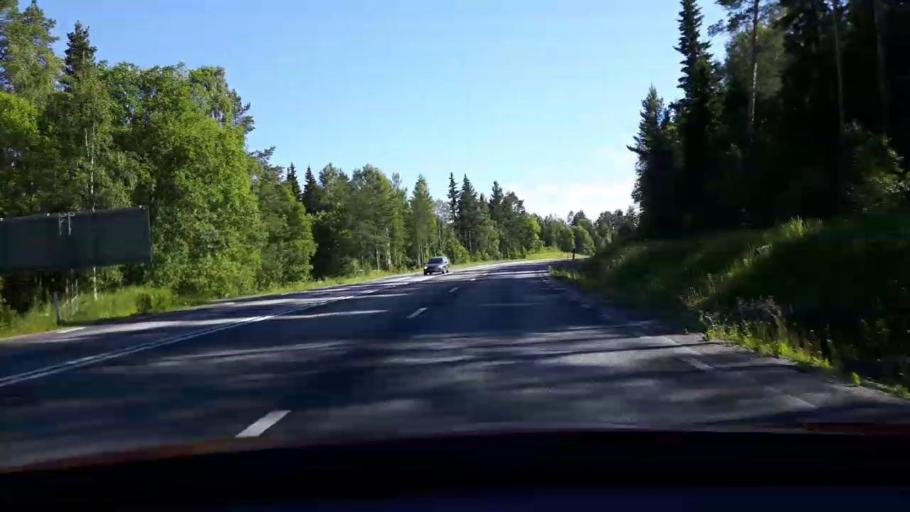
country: SE
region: Jaemtland
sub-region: OEstersunds Kommun
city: Ostersund
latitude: 63.2067
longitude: 14.6839
